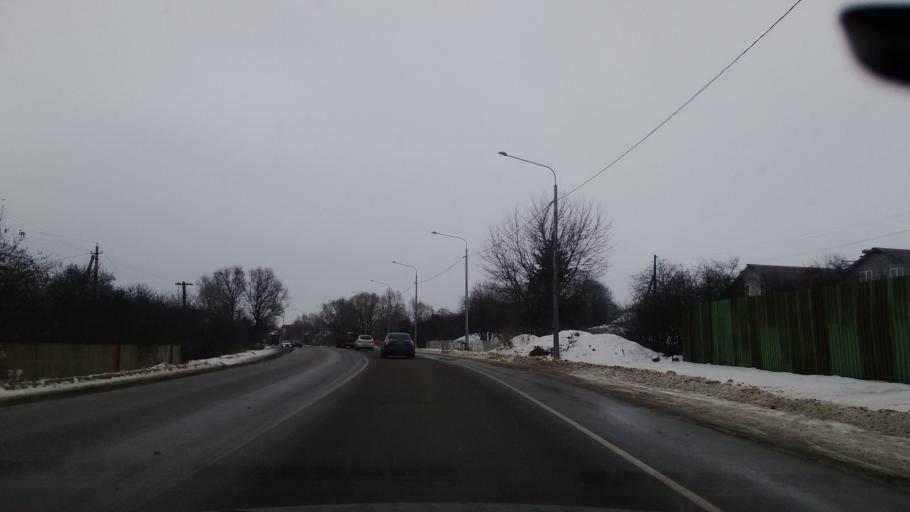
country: RU
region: Tula
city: Borodinskiy
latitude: 54.0257
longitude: 37.8904
